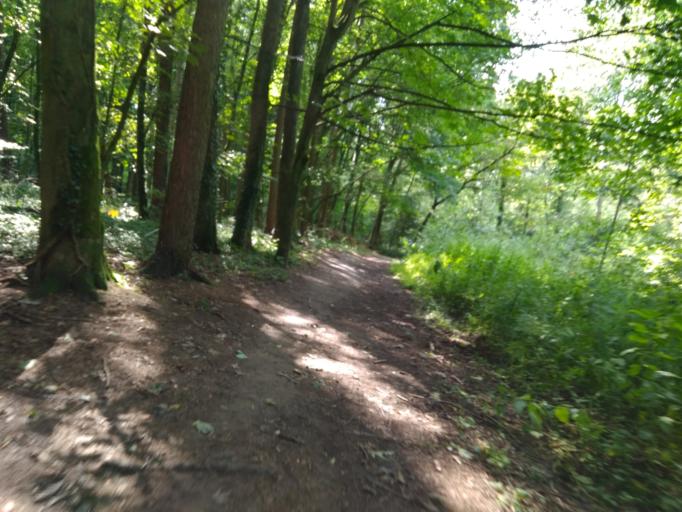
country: DE
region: North Rhine-Westphalia
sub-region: Regierungsbezirk Munster
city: Gladbeck
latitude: 51.6027
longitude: 6.9763
